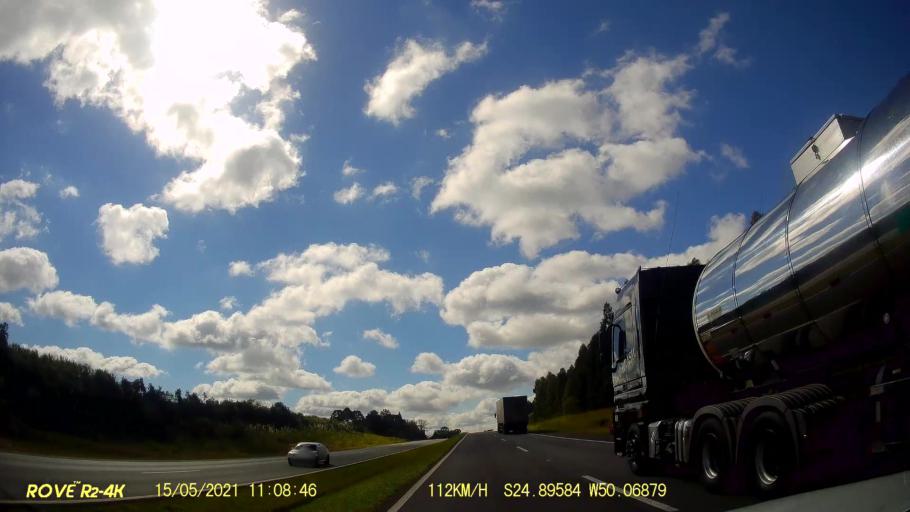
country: BR
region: Parana
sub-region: Carambei
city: Carambei
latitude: -24.8960
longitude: -50.0690
